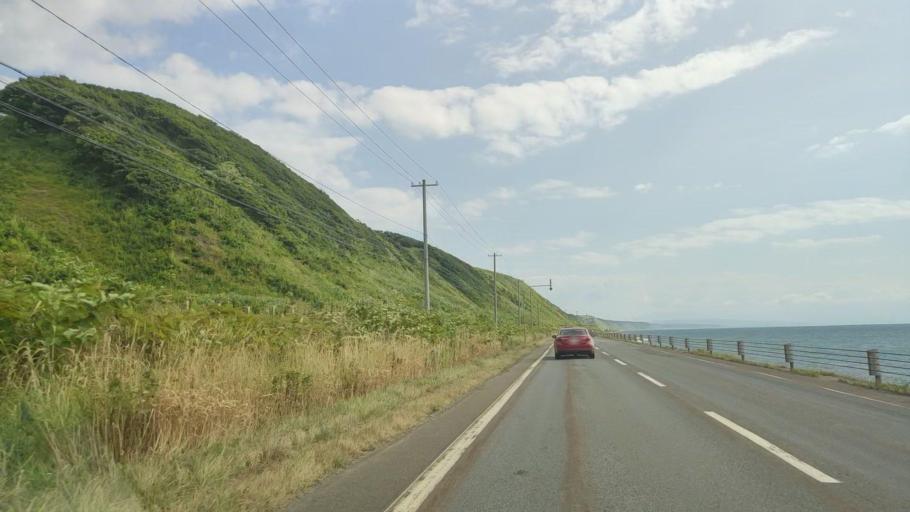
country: JP
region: Hokkaido
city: Rumoi
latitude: 44.0956
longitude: 141.6606
